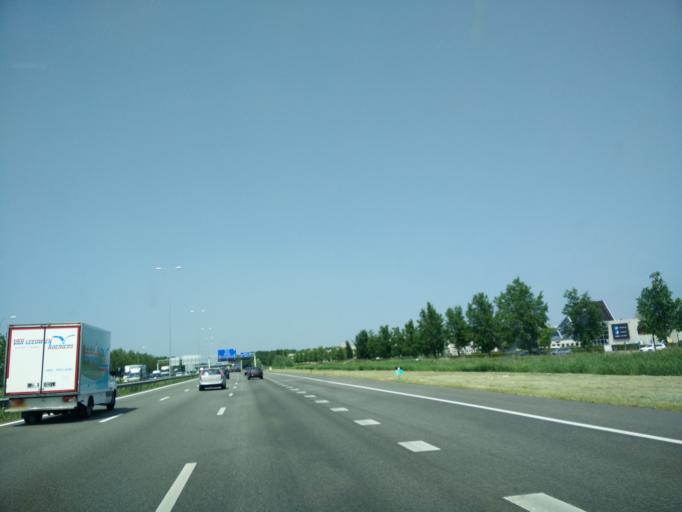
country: NL
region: Utrecht
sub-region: Gemeente Utrecht
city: Lunetten
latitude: 52.0378
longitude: 5.1393
